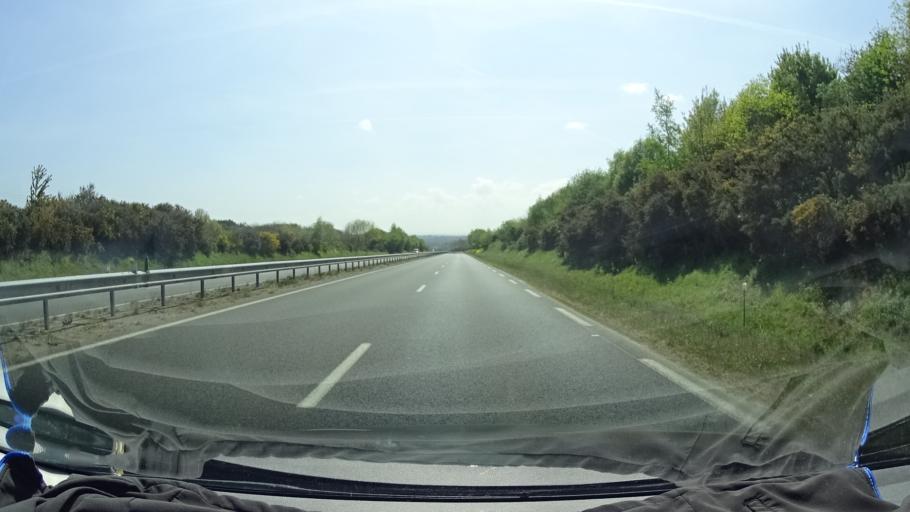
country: FR
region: Brittany
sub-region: Departement des Cotes-d'Armor
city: Plehedel
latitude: 48.7000
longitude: -3.0203
